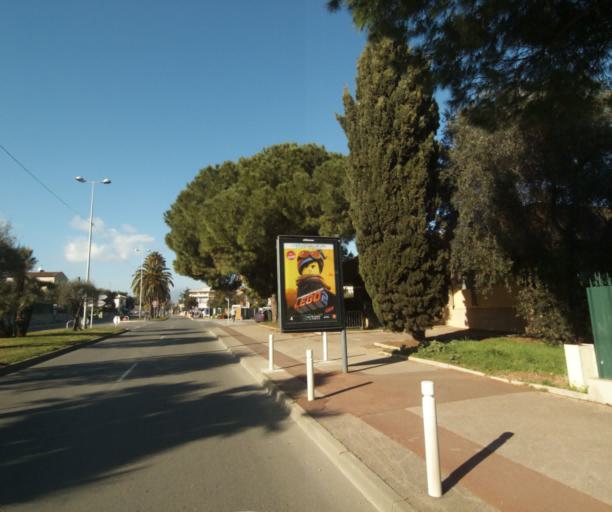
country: FR
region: Provence-Alpes-Cote d'Azur
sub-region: Departement des Alpes-Maritimes
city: Antibes
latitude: 43.5912
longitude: 7.1167
